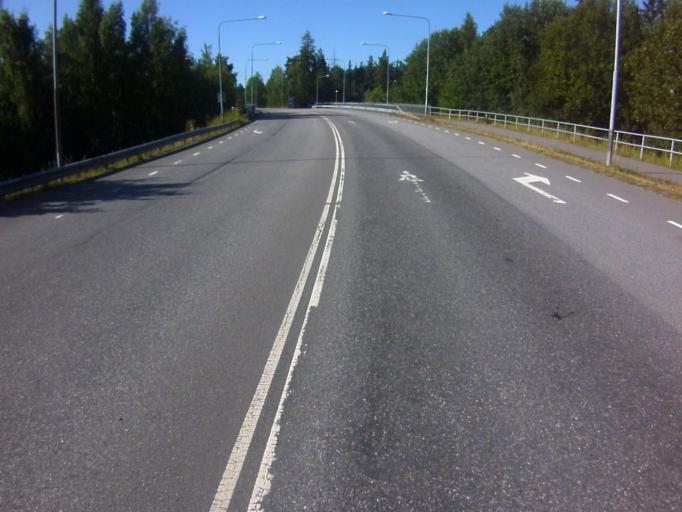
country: SE
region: Soedermanland
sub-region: Eskilstuna Kommun
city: Hallbybrunn
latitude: 59.3980
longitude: 16.4423
